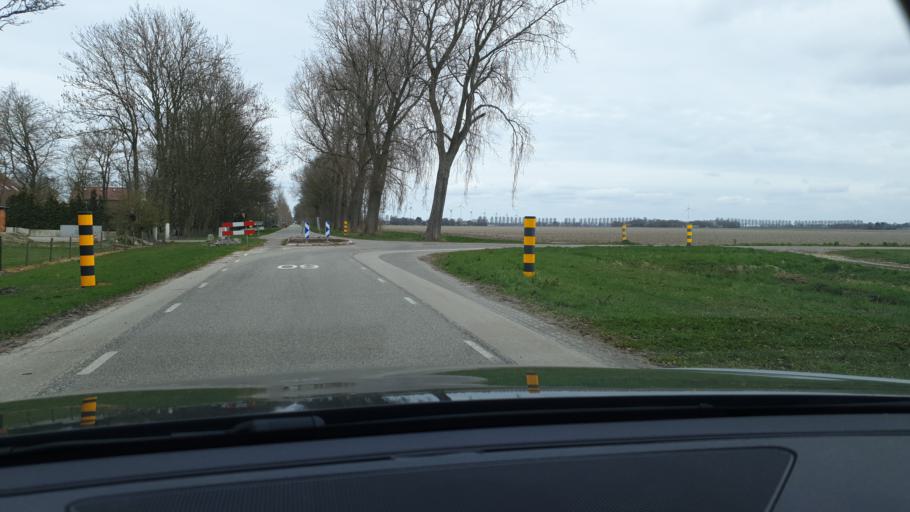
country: NL
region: Flevoland
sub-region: Gemeente Urk
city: Urk
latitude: 52.7389
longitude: 5.6081
